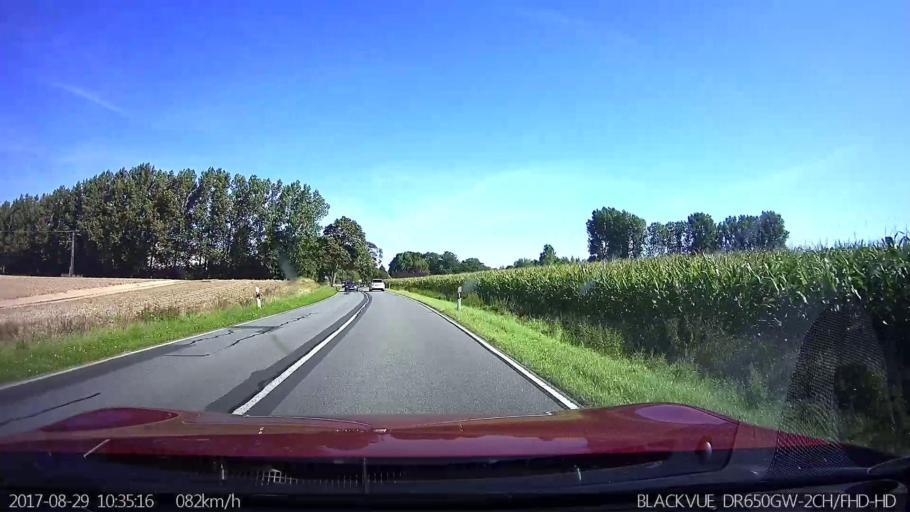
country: DE
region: Mecklenburg-Vorpommern
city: Tribsees
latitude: 54.1356
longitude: 12.7964
